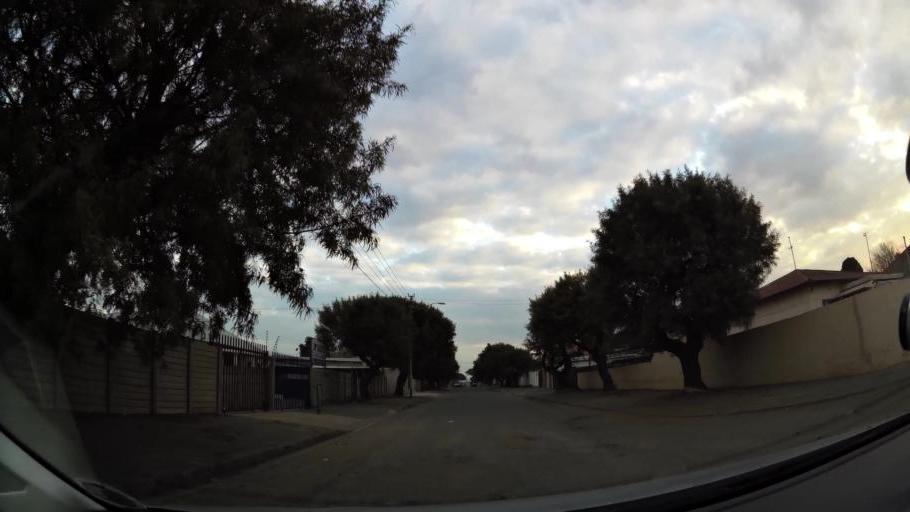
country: ZA
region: Gauteng
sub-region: Ekurhuleni Metropolitan Municipality
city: Germiston
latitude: -26.1959
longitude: 28.1517
